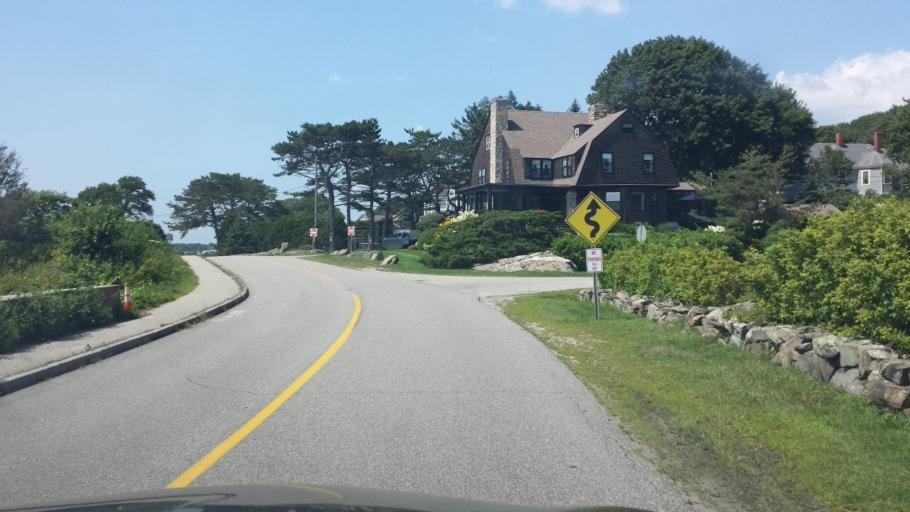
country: US
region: Maine
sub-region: York County
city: Kennebunkport
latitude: 43.3427
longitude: -70.4696
